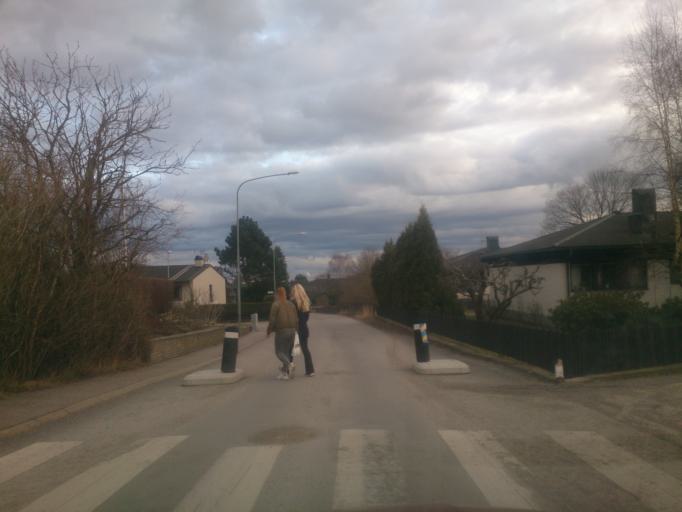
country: SE
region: OEstergoetland
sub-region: Norrkopings Kommun
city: Jursla
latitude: 58.6718
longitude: 16.1857
